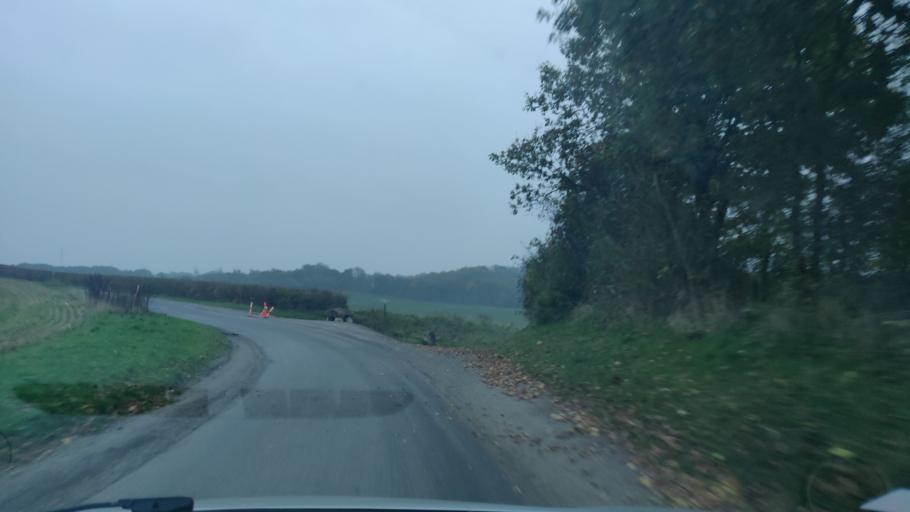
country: DK
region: South Denmark
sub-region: Kolding Kommune
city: Kolding
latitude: 55.5718
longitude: 9.4378
